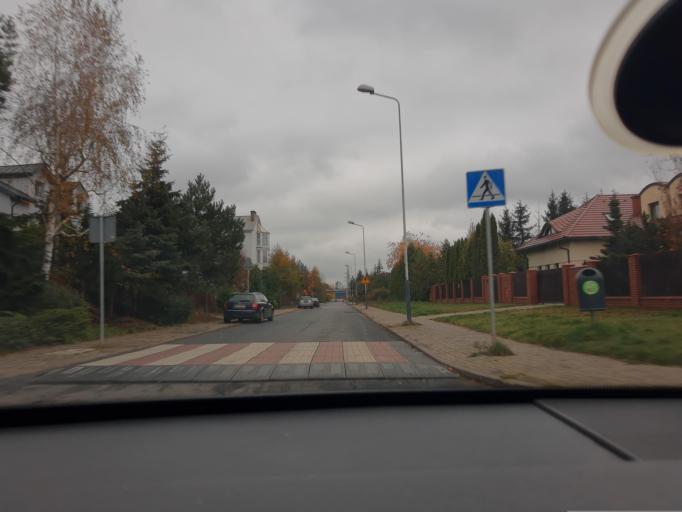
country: PL
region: Lodz Voivodeship
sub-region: Powiat pabianicki
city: Konstantynow Lodzki
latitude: 51.7377
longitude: 19.3753
